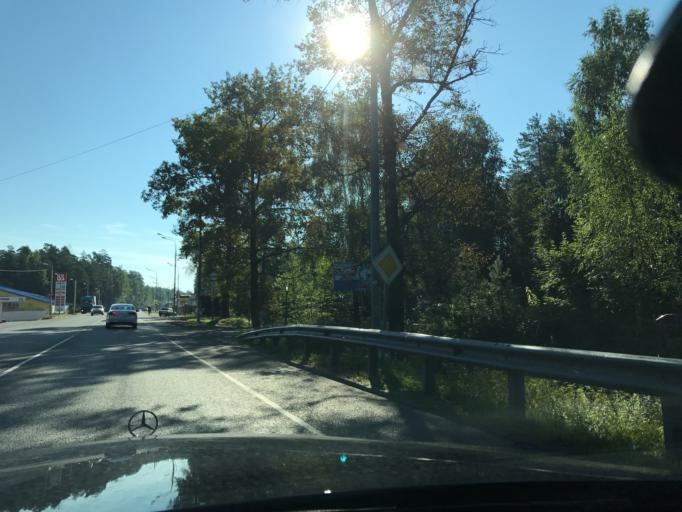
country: RU
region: Moskovskaya
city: Sverdlovskiy
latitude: 55.9278
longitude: 38.1477
